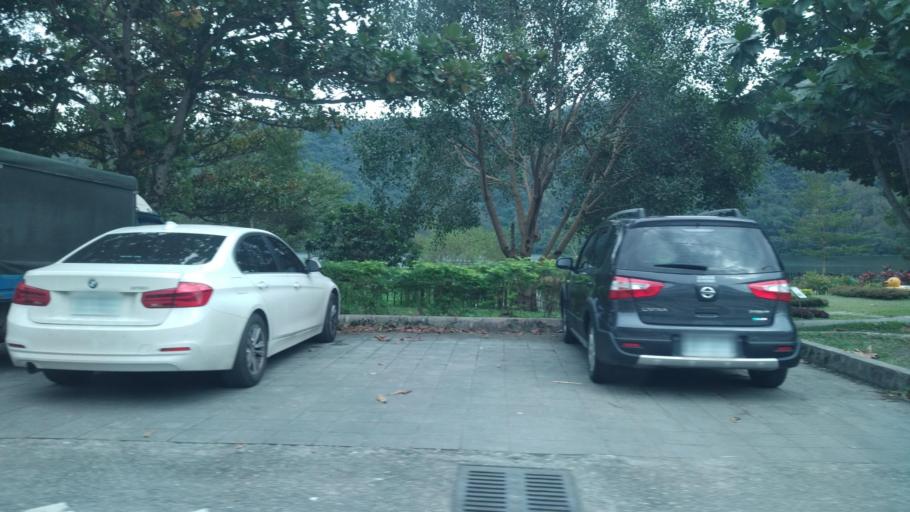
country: TW
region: Taiwan
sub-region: Hualien
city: Hualian
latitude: 23.9264
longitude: 121.5055
